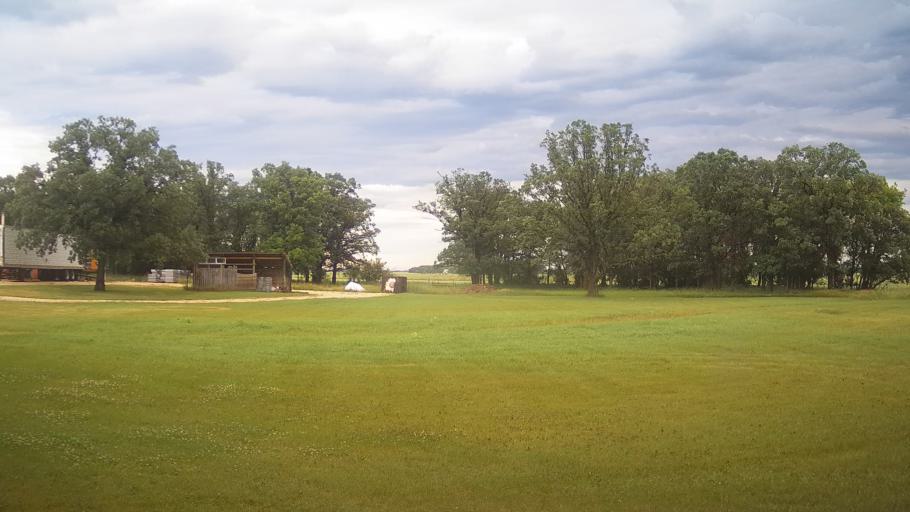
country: CA
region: Manitoba
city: Stonewall
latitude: 50.1257
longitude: -97.4743
